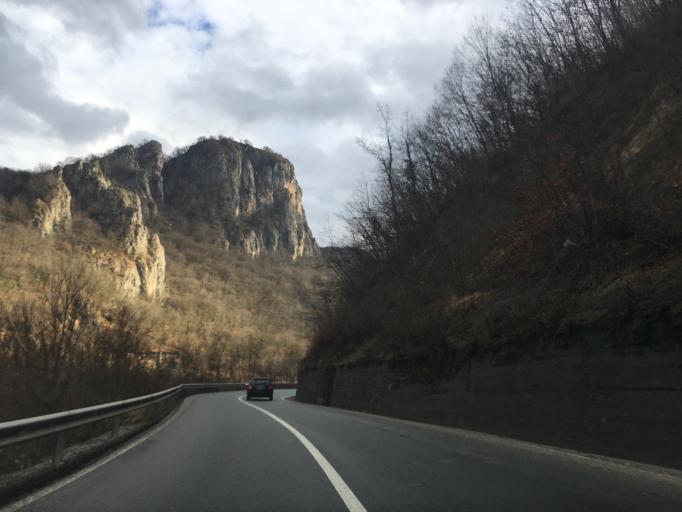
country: RS
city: Sokolovo Brdo
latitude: 43.1544
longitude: 19.7788
